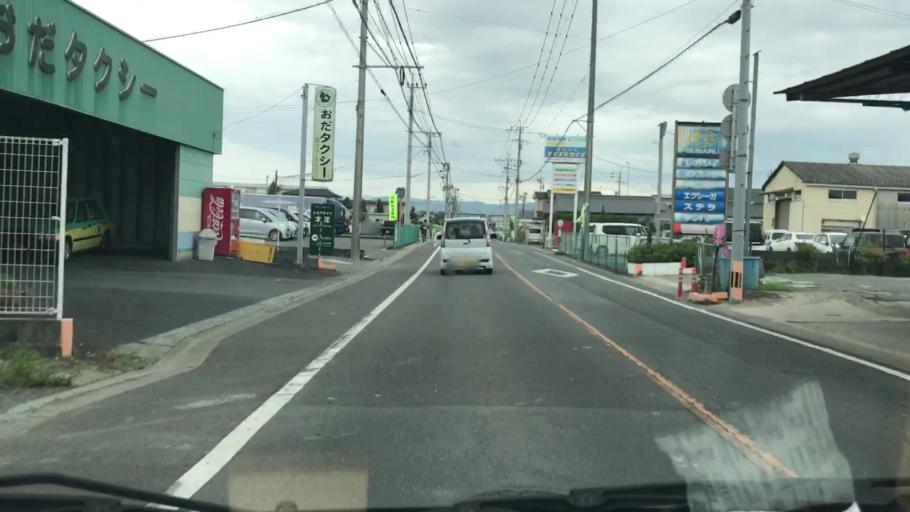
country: JP
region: Saga Prefecture
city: Saga-shi
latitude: 33.2296
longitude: 130.2939
